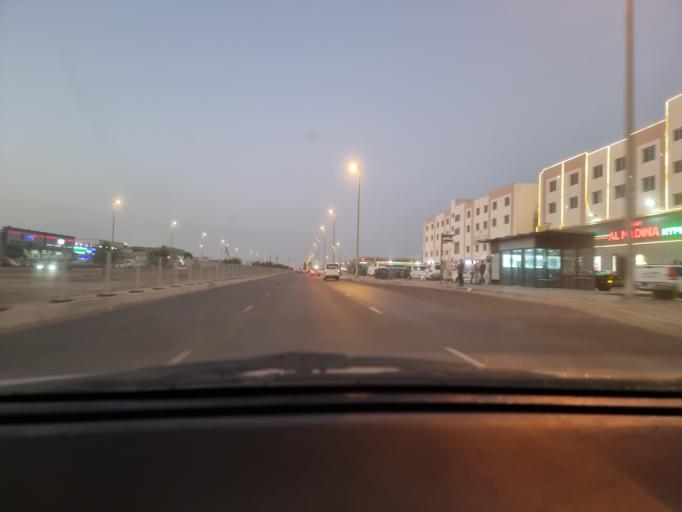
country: AE
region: Abu Dhabi
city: Abu Dhabi
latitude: 24.3616
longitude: 54.5167
